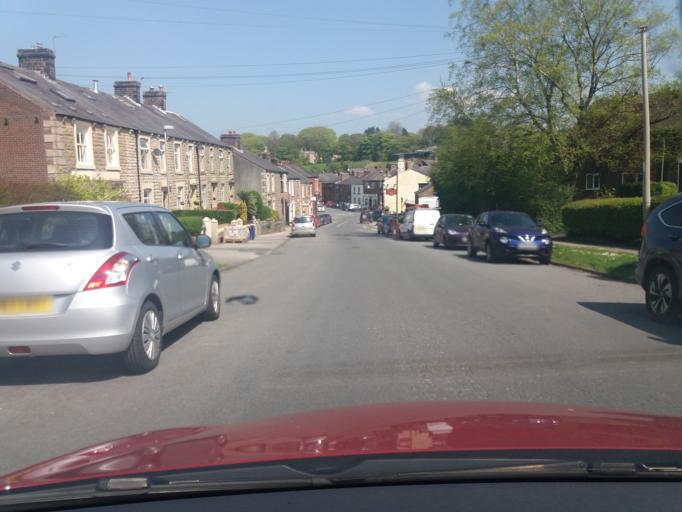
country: GB
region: England
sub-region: Lancashire
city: Chorley
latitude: 53.6847
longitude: -2.6076
